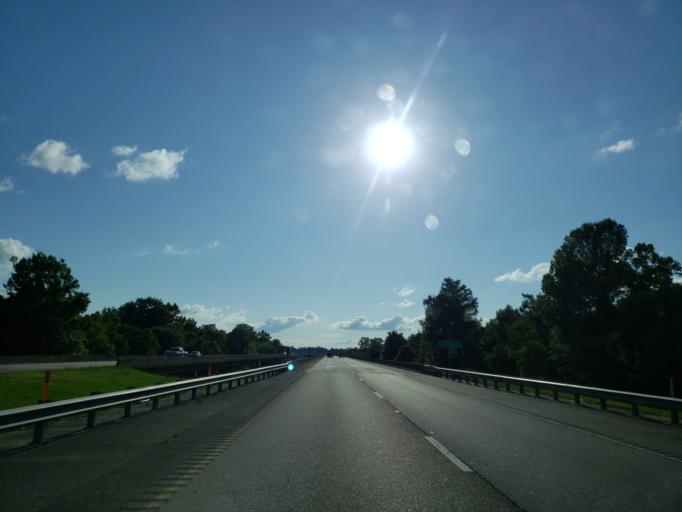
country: US
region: Mississippi
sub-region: Forrest County
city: Petal
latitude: 31.3596
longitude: -89.2793
